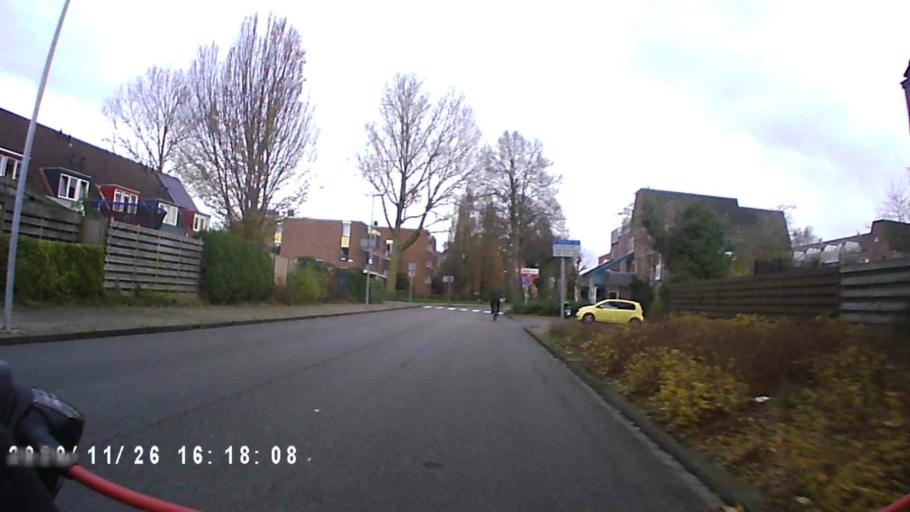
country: NL
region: Groningen
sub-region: Gemeente Groningen
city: Oosterpark
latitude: 53.2400
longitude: 6.6248
